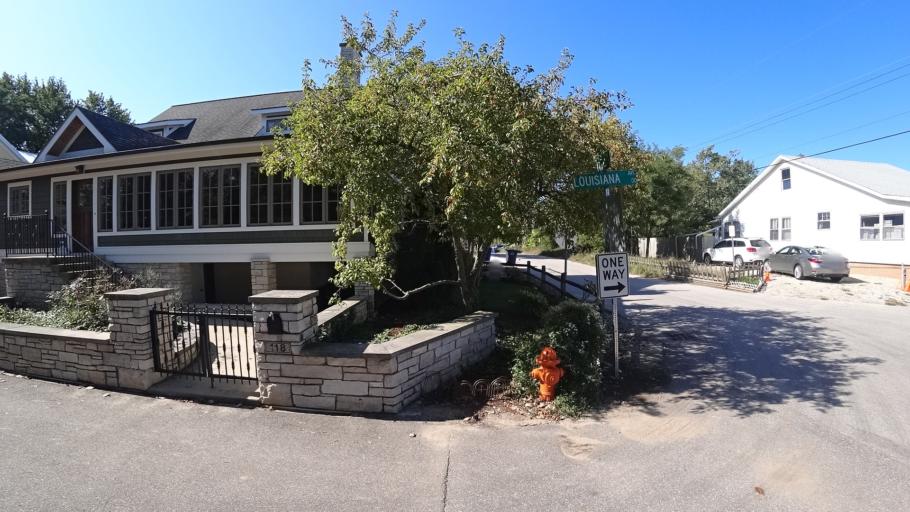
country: US
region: Indiana
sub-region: LaPorte County
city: Michigan City
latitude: 41.7301
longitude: -86.8914
